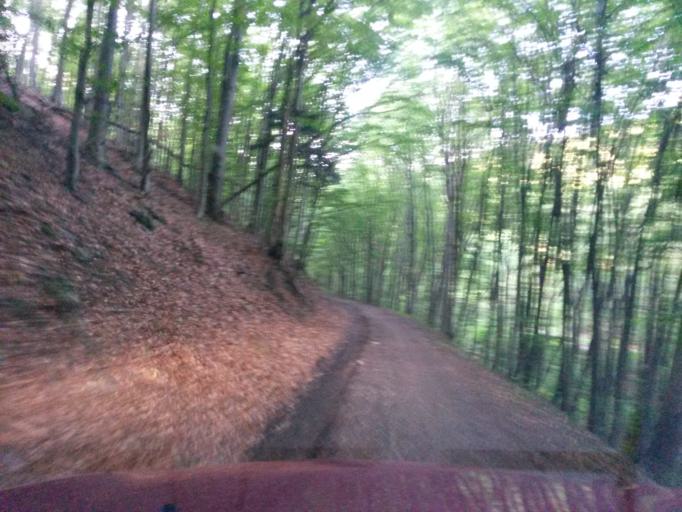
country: SK
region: Kosicky
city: Moldava nad Bodvou
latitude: 48.7352
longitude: 21.0640
